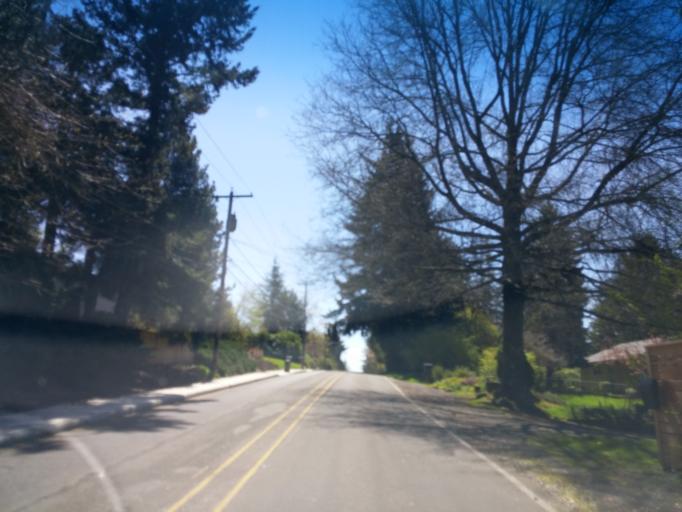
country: US
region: Oregon
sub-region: Washington County
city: West Haven
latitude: 45.5207
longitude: -122.7696
